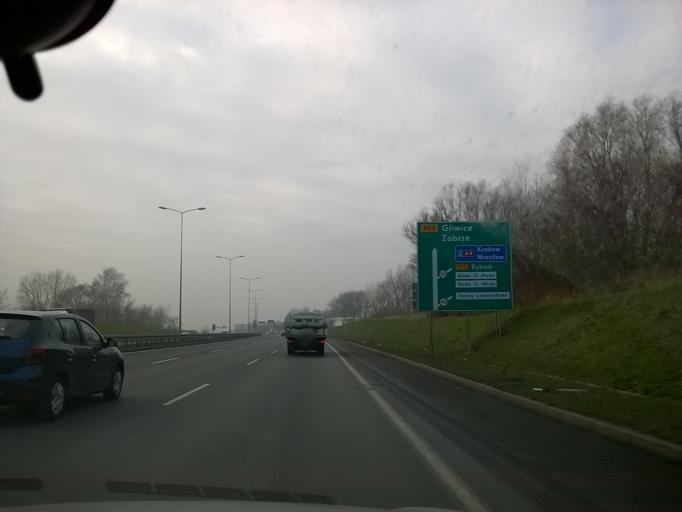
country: PL
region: Silesian Voivodeship
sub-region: Swietochlowice
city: Swietochlowice
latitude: 50.3007
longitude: 18.8747
